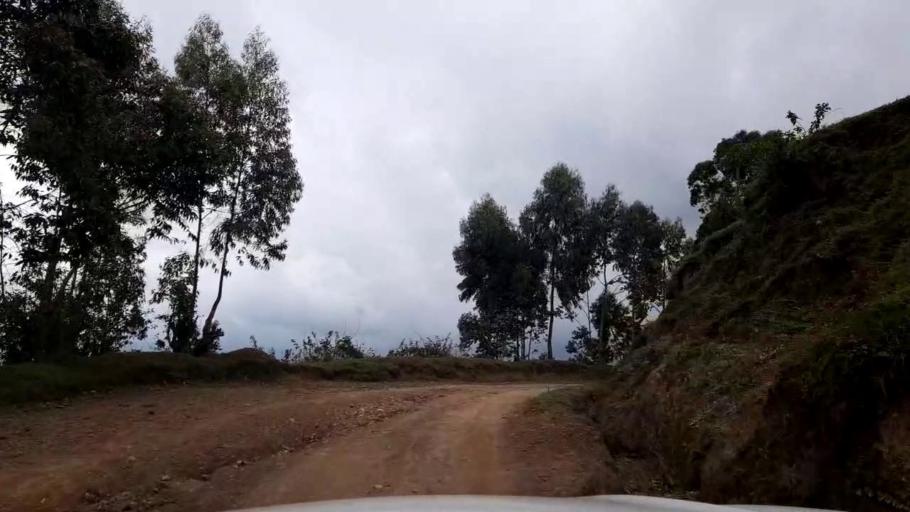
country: RW
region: Western Province
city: Kibuye
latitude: -1.9663
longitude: 29.4860
